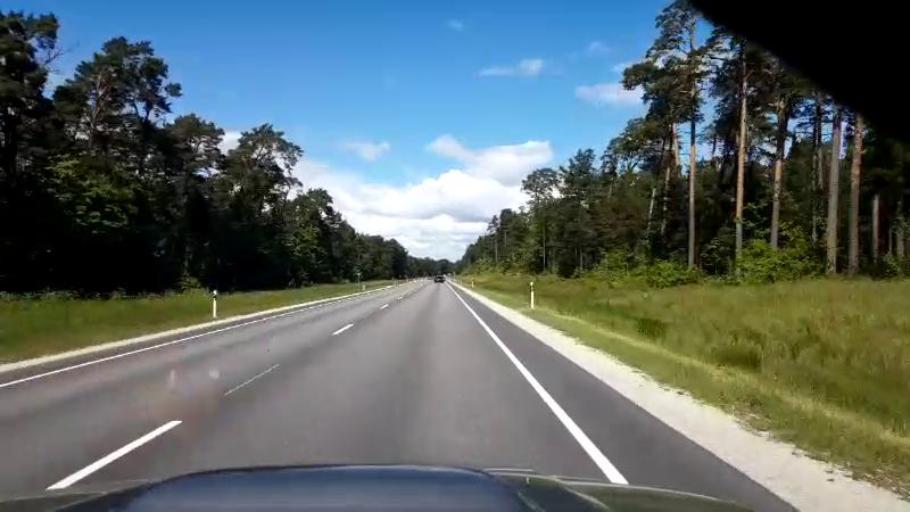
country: EE
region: Paernumaa
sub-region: Paernu linn
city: Parnu
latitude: 58.1975
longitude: 24.4873
